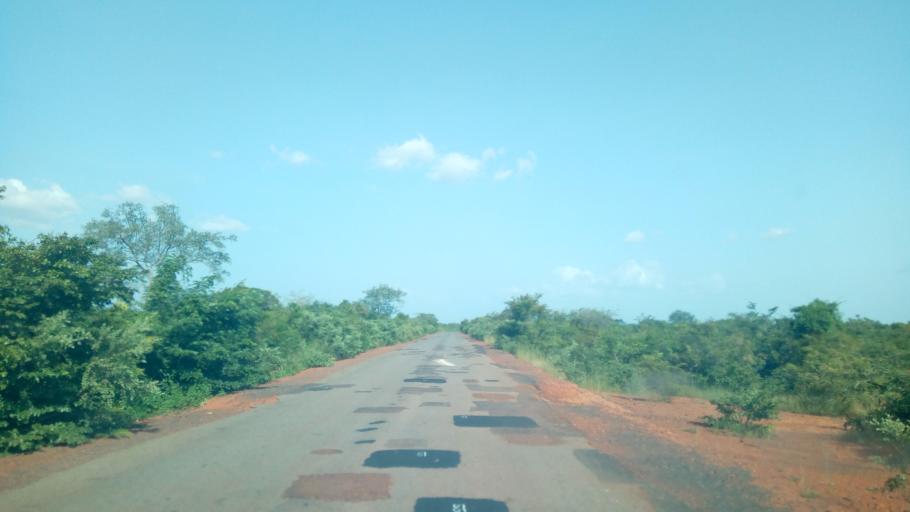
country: ML
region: Sikasso
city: Yorosso
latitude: 12.2122
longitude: -4.9039
